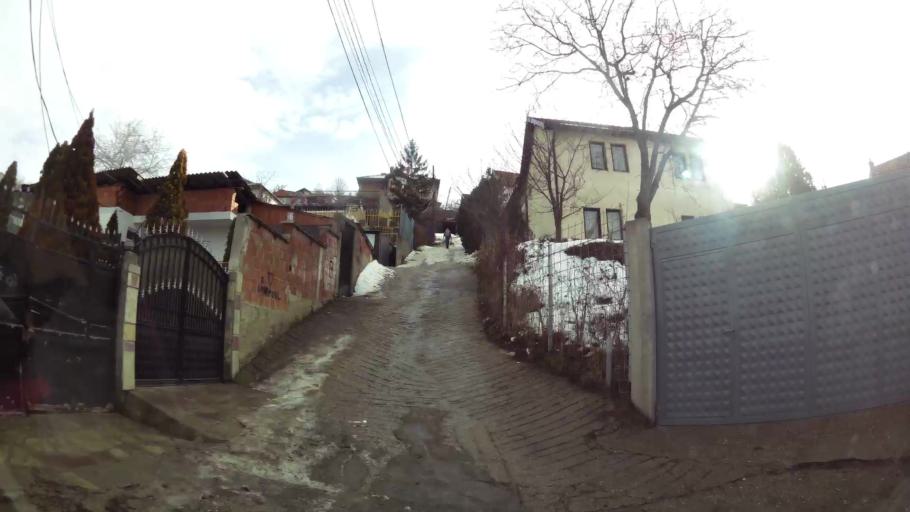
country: XK
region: Pristina
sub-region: Komuna e Prishtines
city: Pristina
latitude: 42.6732
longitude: 21.1757
